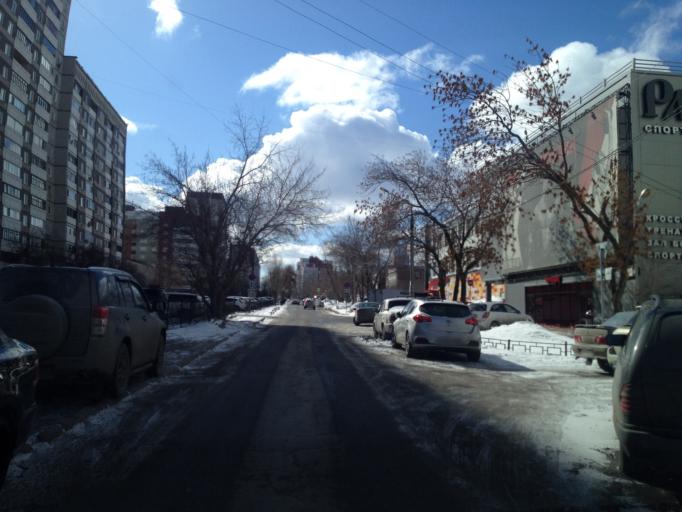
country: RU
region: Sverdlovsk
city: Yekaterinburg
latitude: 56.8140
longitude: 60.5966
